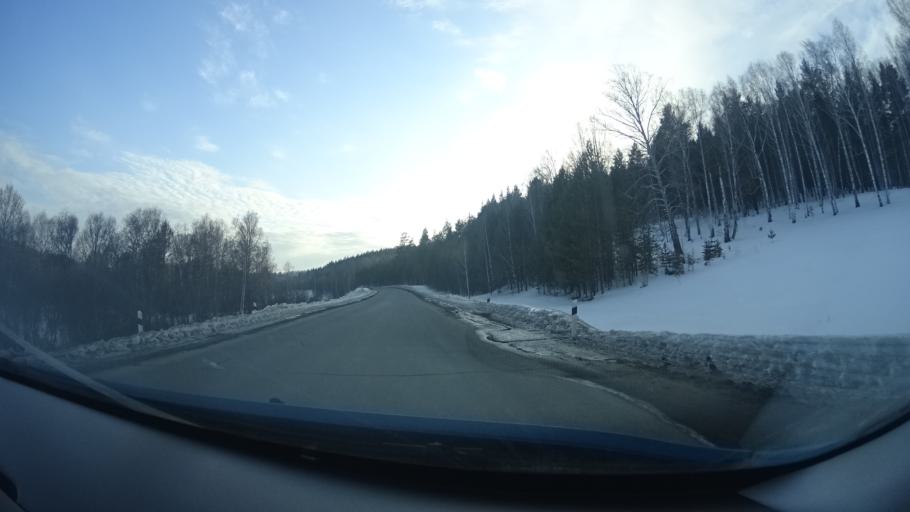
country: RU
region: Bashkortostan
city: Abzakovo
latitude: 53.4537
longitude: 58.3155
